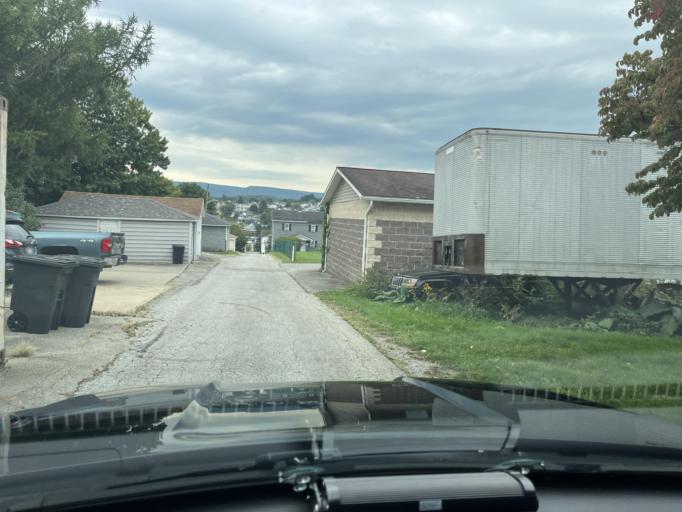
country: US
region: Pennsylvania
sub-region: Fayette County
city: South Uniontown
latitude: 39.8976
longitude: -79.7403
